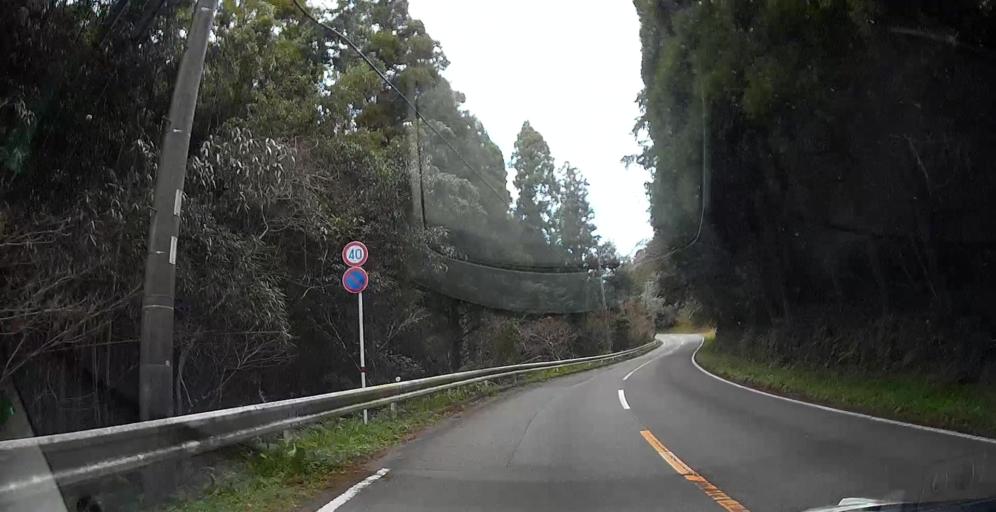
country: JP
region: Kumamoto
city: Yatsushiro
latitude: 32.3699
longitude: 130.5045
